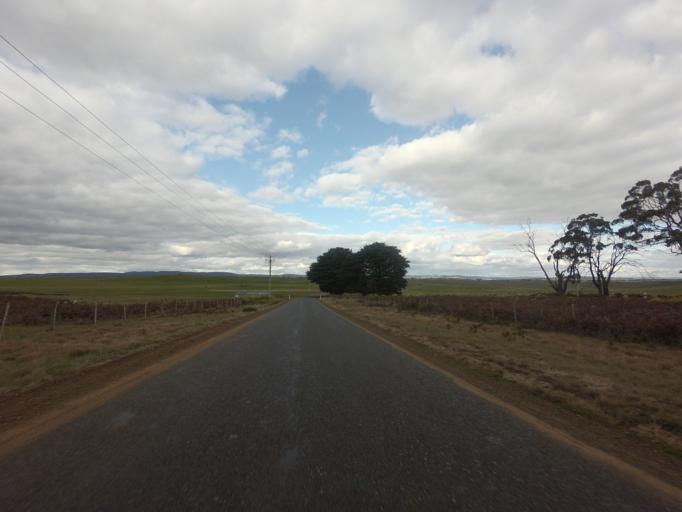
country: AU
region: Tasmania
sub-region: Northern Midlands
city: Evandale
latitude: -41.8935
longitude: 147.4159
